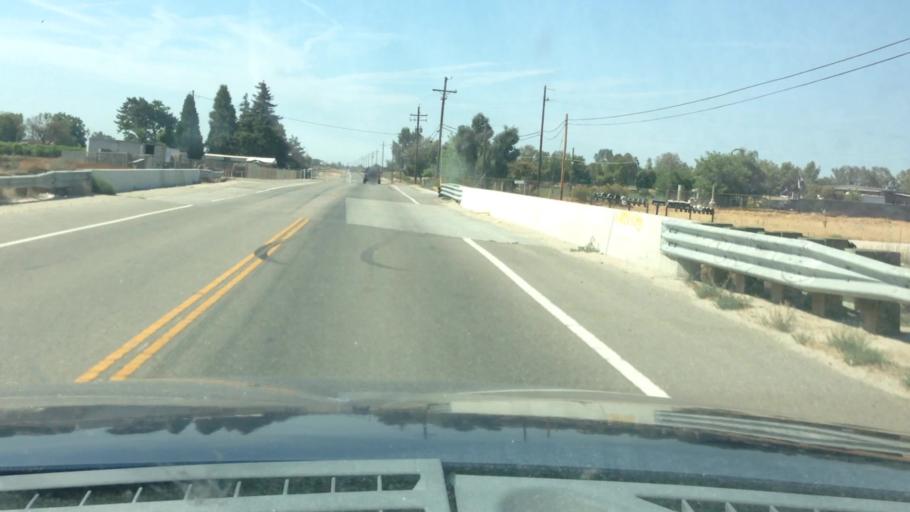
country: US
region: California
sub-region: Fresno County
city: Parlier
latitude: 36.5988
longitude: -119.5569
